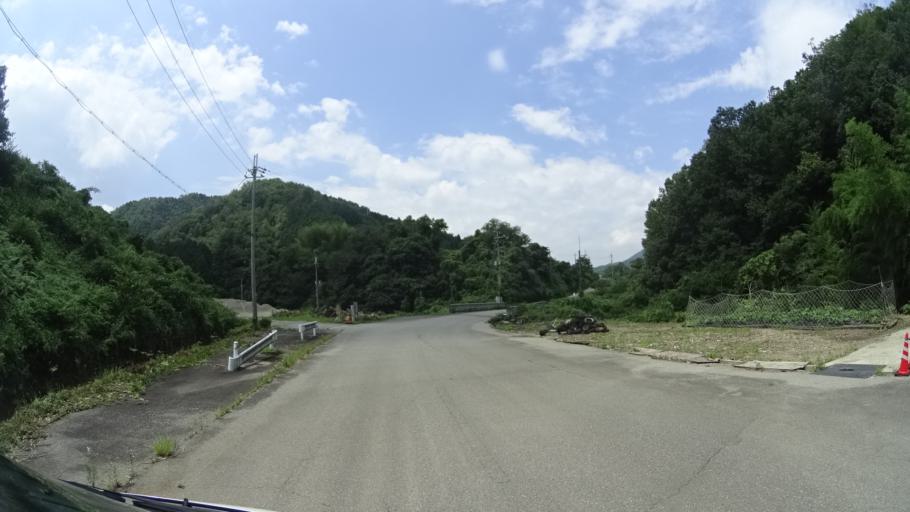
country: JP
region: Hyogo
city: Sasayama
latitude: 35.1669
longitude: 135.2653
